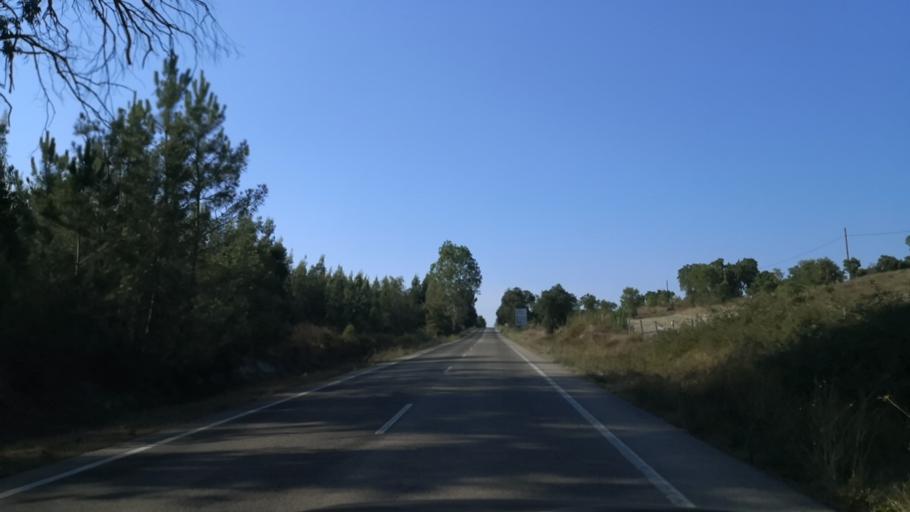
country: PT
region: Santarem
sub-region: Almeirim
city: Fazendas de Almeirim
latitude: 39.0724
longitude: -8.5656
